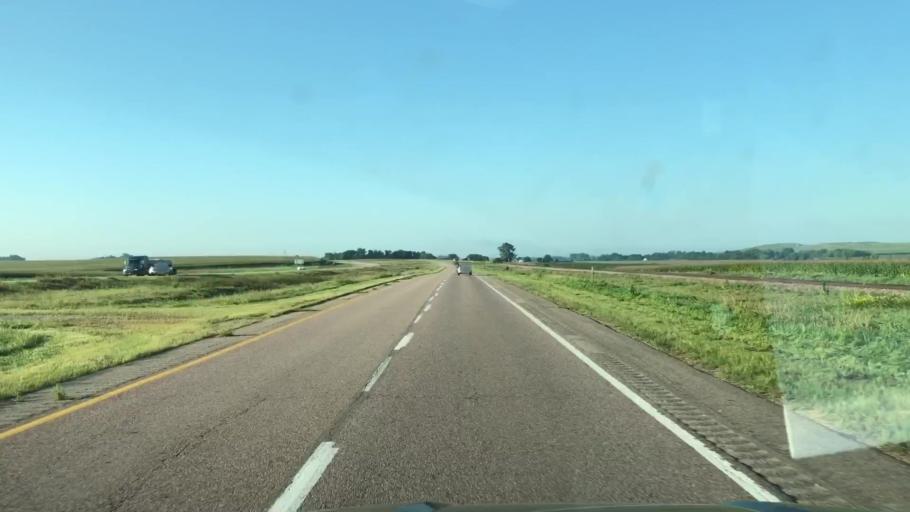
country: US
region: Iowa
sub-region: O'Brien County
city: Sheldon
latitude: 43.1464
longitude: -95.8789
